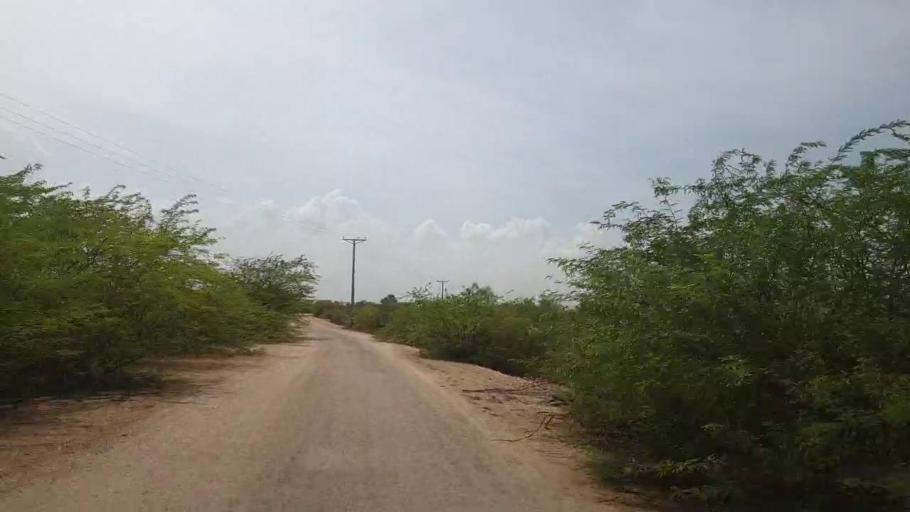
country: PK
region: Sindh
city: Kot Diji
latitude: 27.2371
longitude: 69.0821
